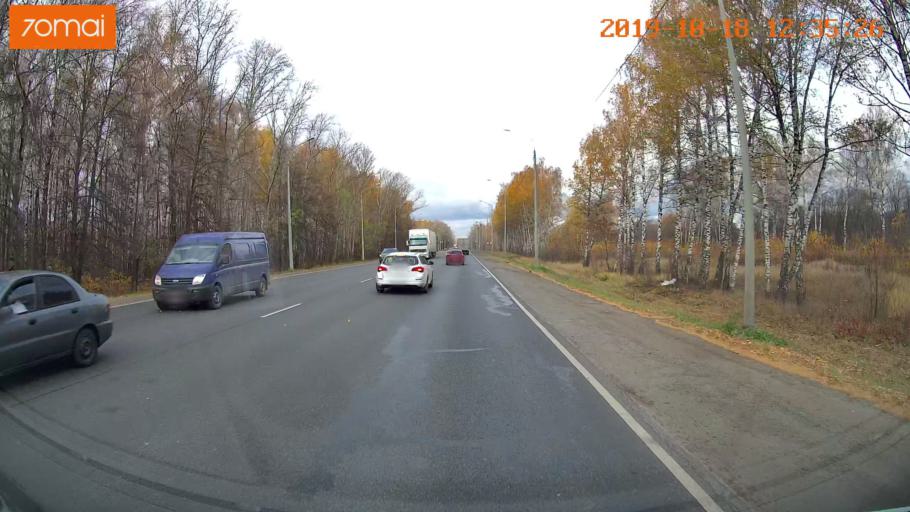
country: RU
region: Rjazan
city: Ryazan'
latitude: 54.6245
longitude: 39.6357
